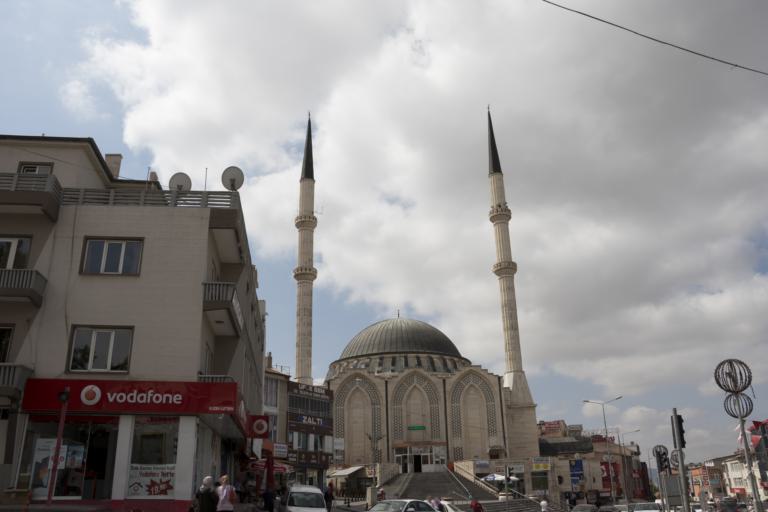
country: TR
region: Kayseri
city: Develi
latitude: 38.3886
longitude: 35.4931
